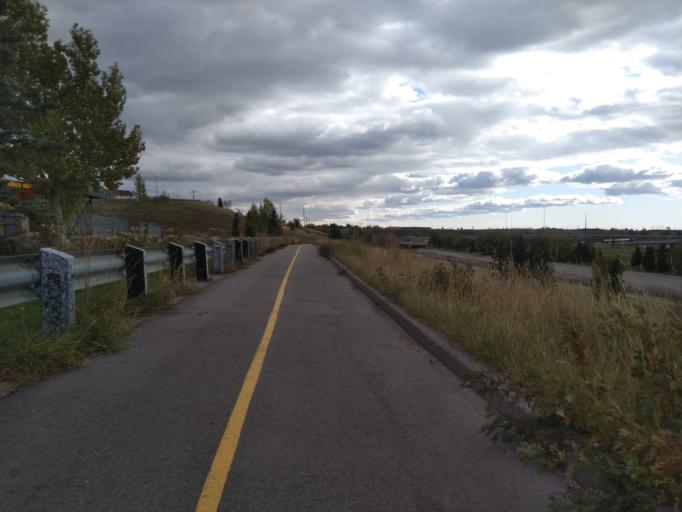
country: CA
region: Alberta
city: Calgary
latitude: 51.0417
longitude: -114.0051
